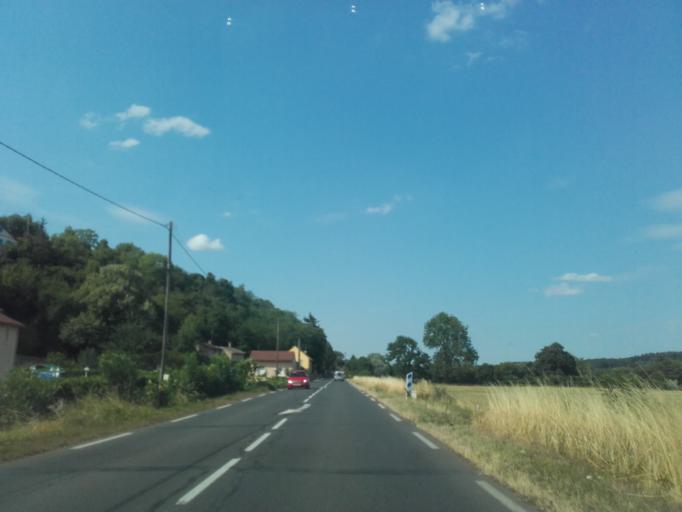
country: FR
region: Bourgogne
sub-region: Departement de Saone-et-Loire
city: Cluny
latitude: 46.4467
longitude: 4.6653
